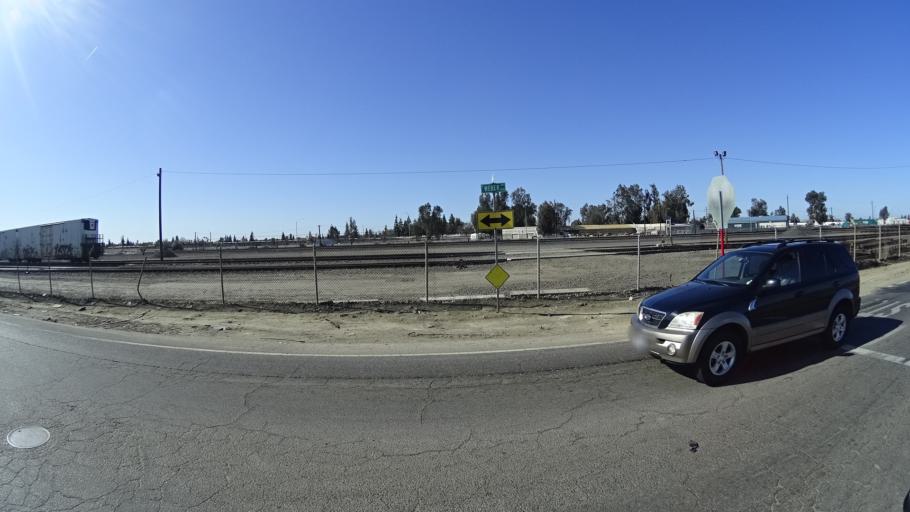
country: US
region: California
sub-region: Fresno County
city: West Park
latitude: 36.7920
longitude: -119.8579
